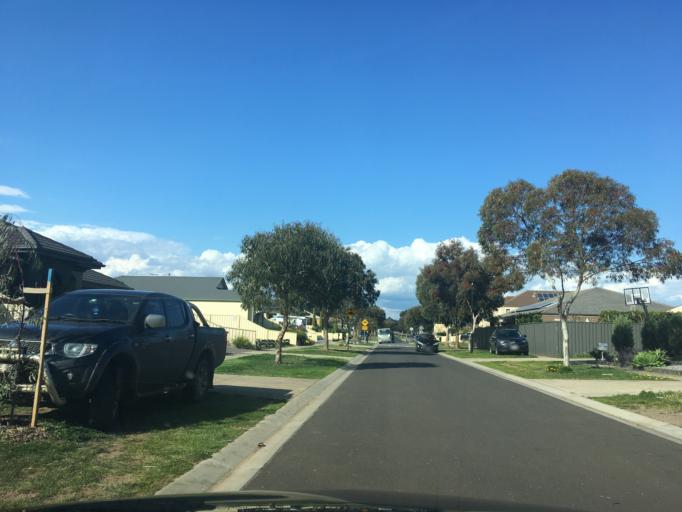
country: AU
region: Victoria
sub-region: Wyndham
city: Williams Landing
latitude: -37.8818
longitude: 144.7303
